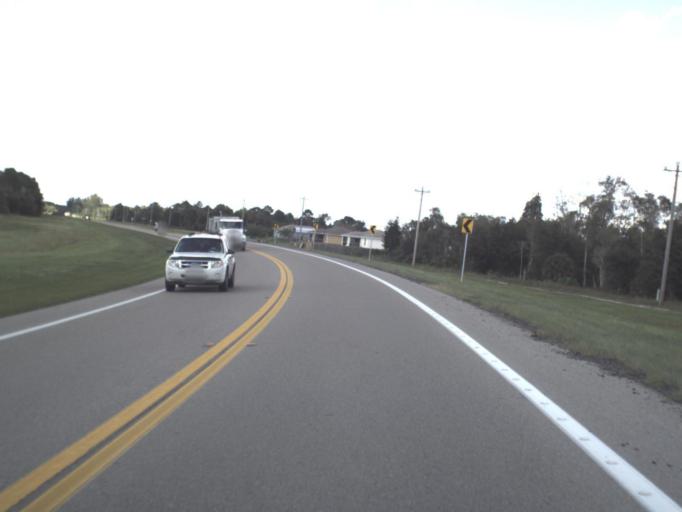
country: US
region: Florida
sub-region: Lee County
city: Lehigh Acres
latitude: 26.5449
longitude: -81.6369
